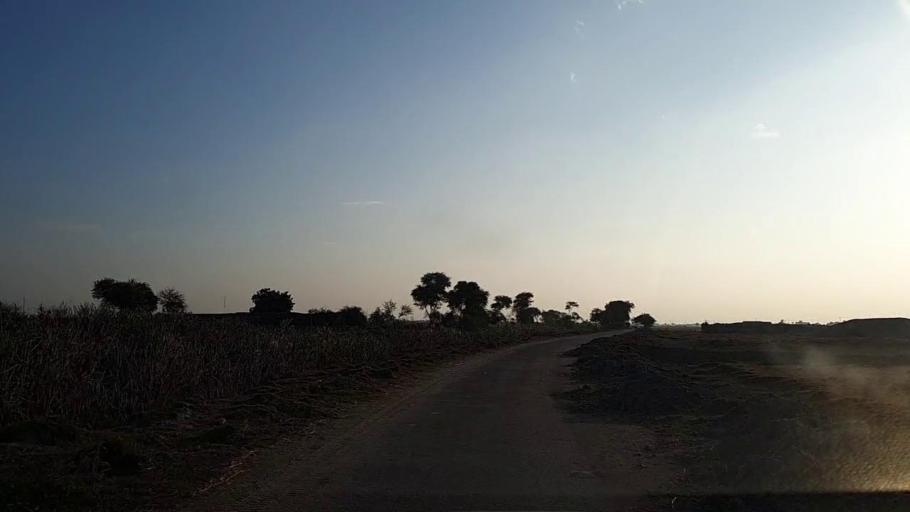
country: PK
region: Sindh
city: Sanghar
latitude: 26.2659
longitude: 68.9813
